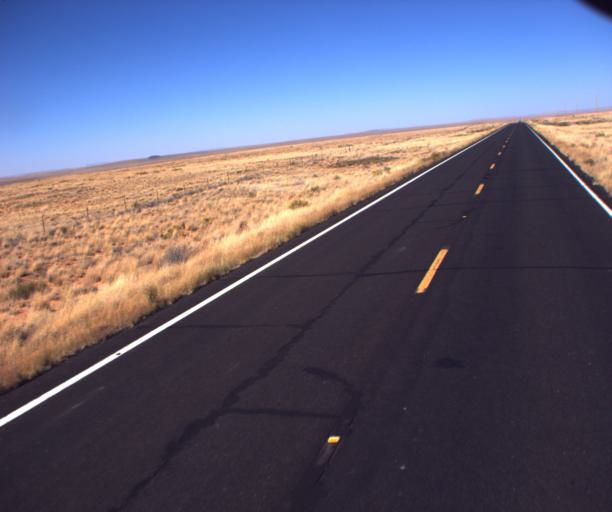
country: US
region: Arizona
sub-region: Navajo County
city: Dilkon
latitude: 35.5340
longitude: -110.4467
